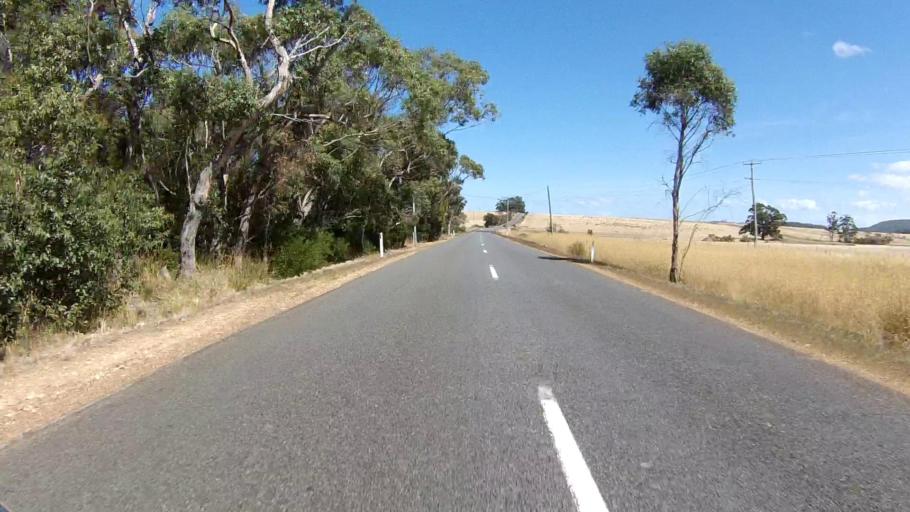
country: AU
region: Tasmania
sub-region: Sorell
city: Sorell
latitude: -42.2447
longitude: 148.0109
